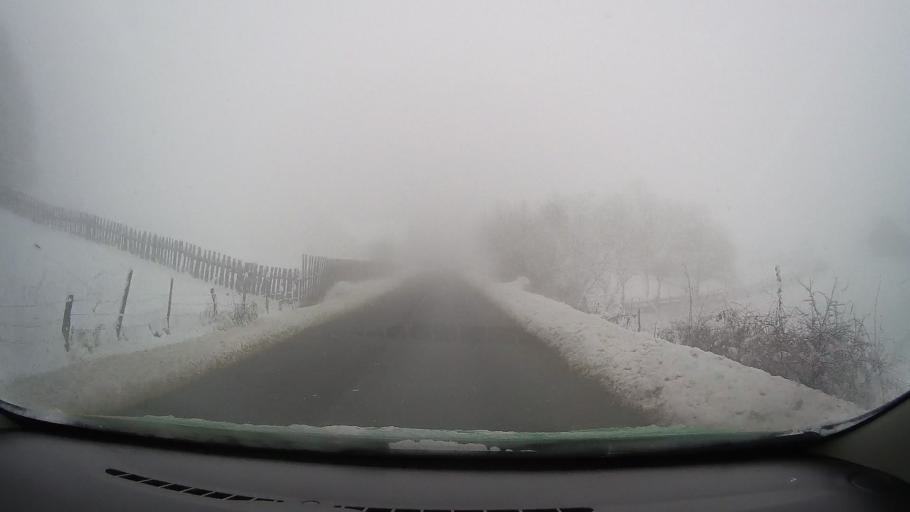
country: RO
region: Sibiu
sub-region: Comuna Jina
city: Jina
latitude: 45.7942
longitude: 23.7018
